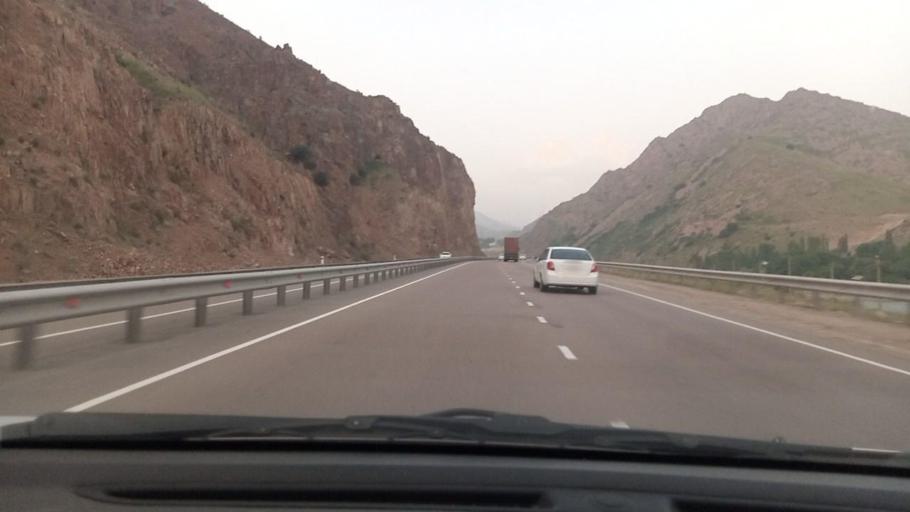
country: UZ
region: Toshkent
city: Angren
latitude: 41.1165
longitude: 70.3427
